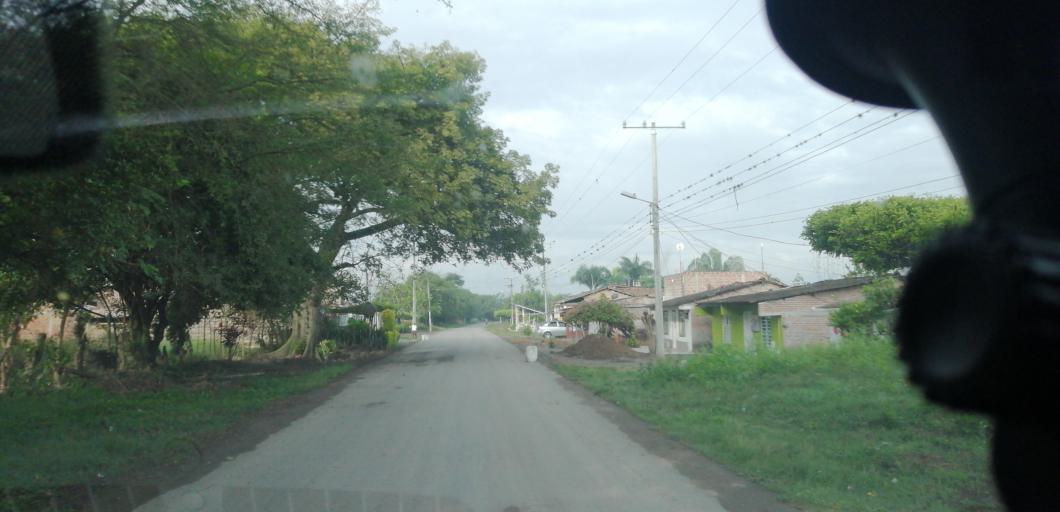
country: CO
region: Valle del Cauca
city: Palmira
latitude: 3.5368
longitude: -76.3532
